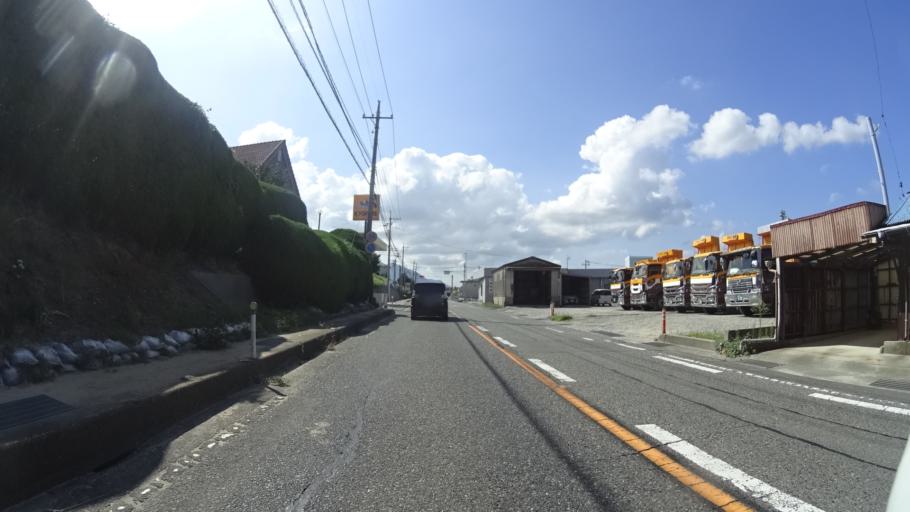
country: JP
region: Yamaguchi
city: Shimonoseki
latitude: 34.1646
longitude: 130.9270
